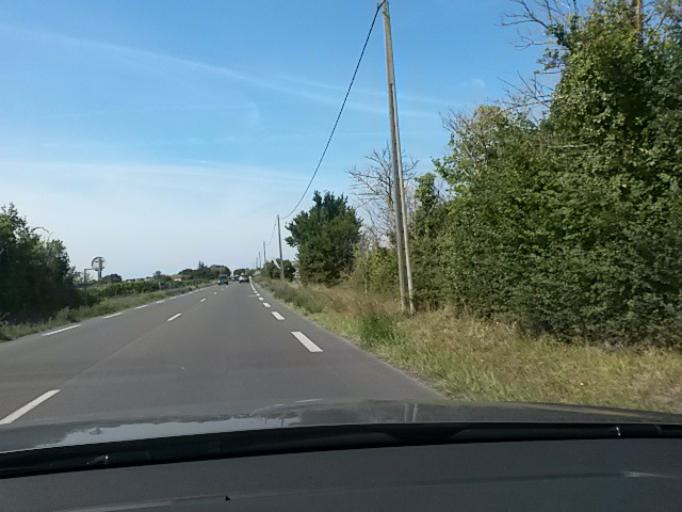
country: FR
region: Poitou-Charentes
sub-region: Departement de la Charente-Maritime
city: Dolus-d'Oleron
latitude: 45.9503
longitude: -1.3292
